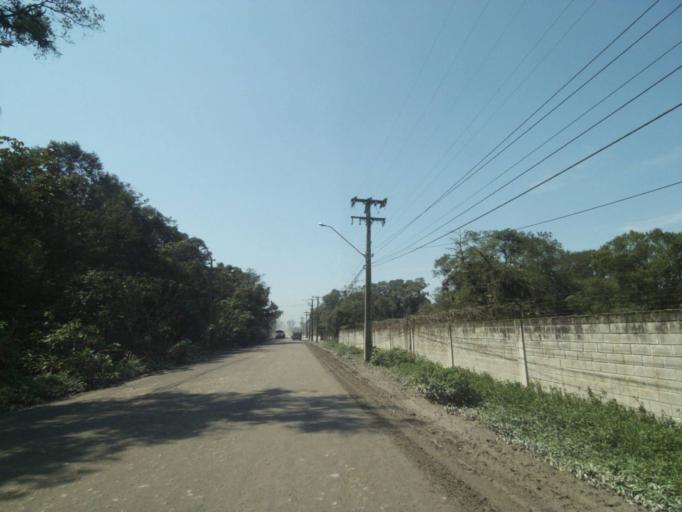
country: BR
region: Parana
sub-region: Paranagua
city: Paranagua
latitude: -25.5462
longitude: -48.5720
